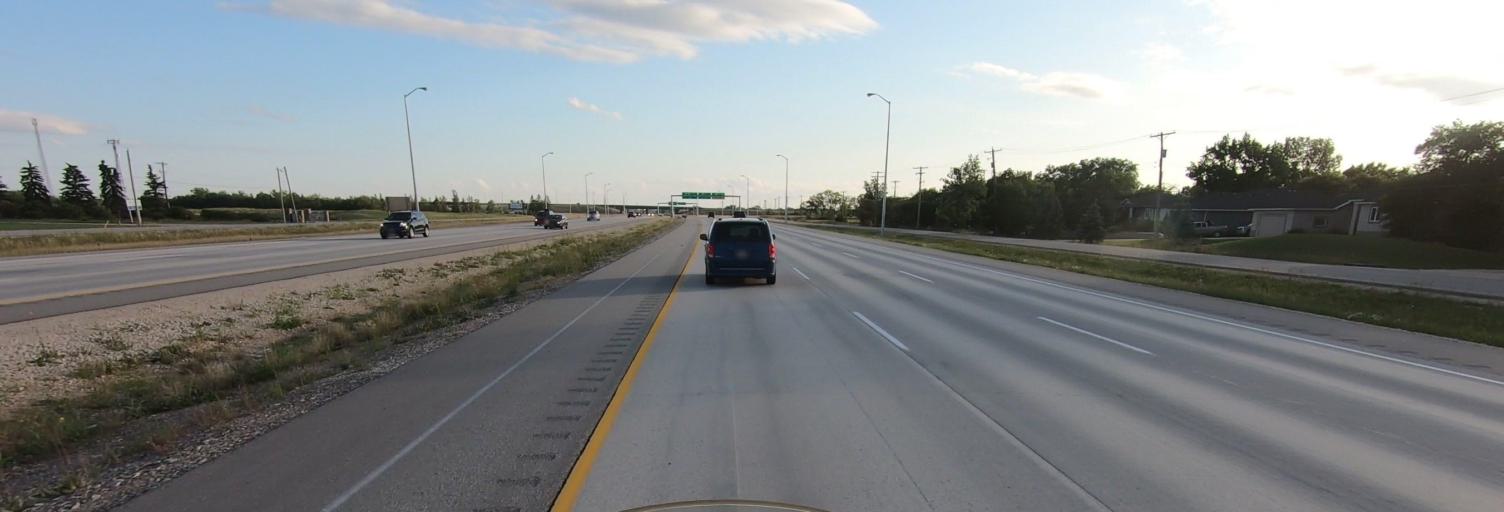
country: CA
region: Manitoba
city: Winnipeg
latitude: 49.9585
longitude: -97.0231
